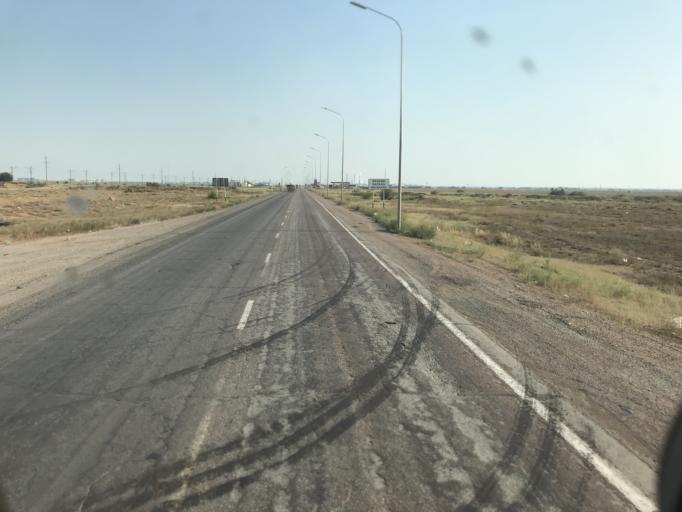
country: KZ
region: Qaraghandy
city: Balqash
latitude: 46.8839
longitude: 74.9489
